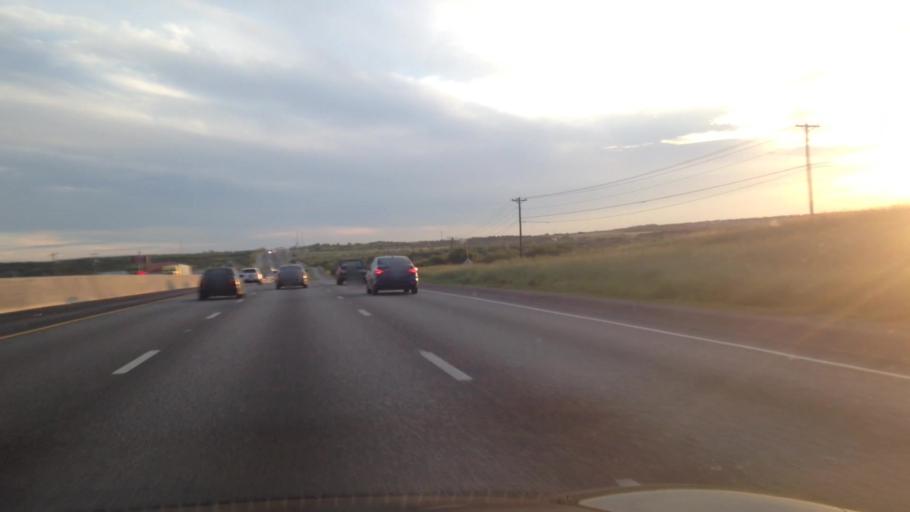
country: US
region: Texas
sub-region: Guadalupe County
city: Lake Dunlap
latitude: 29.7780
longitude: -98.0355
